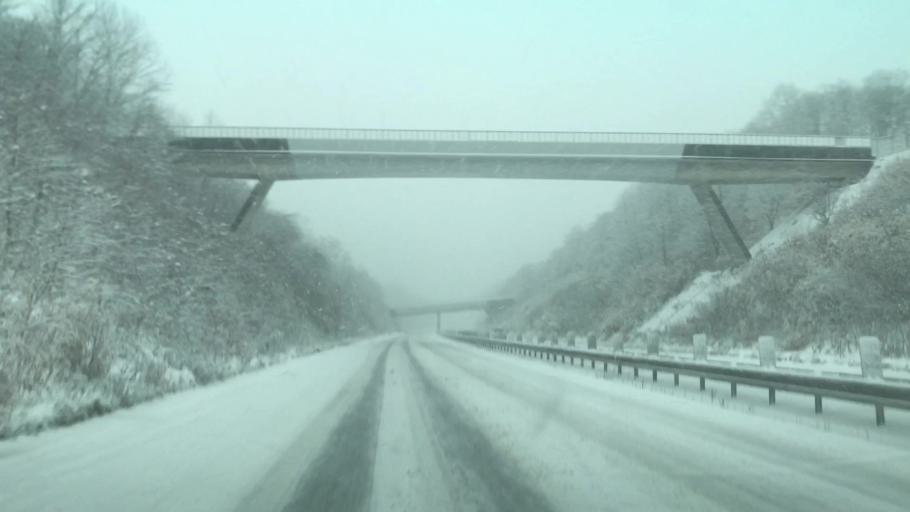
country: JP
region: Hokkaido
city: Muroran
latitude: 42.4369
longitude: 141.1320
